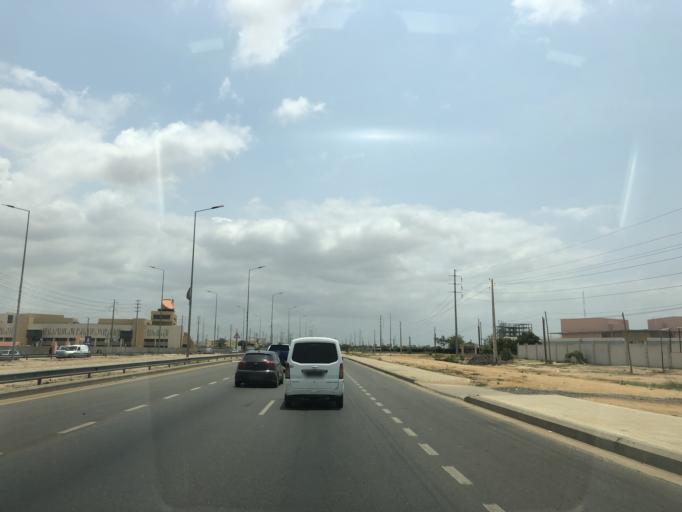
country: AO
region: Luanda
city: Luanda
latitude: -8.9585
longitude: 13.2572
